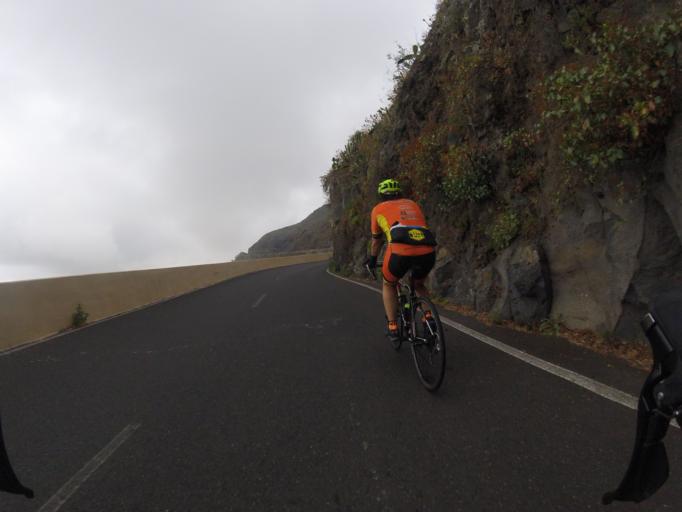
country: ES
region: Canary Islands
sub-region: Provincia de Santa Cruz de Tenerife
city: Guimar
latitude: 28.2944
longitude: -16.4092
